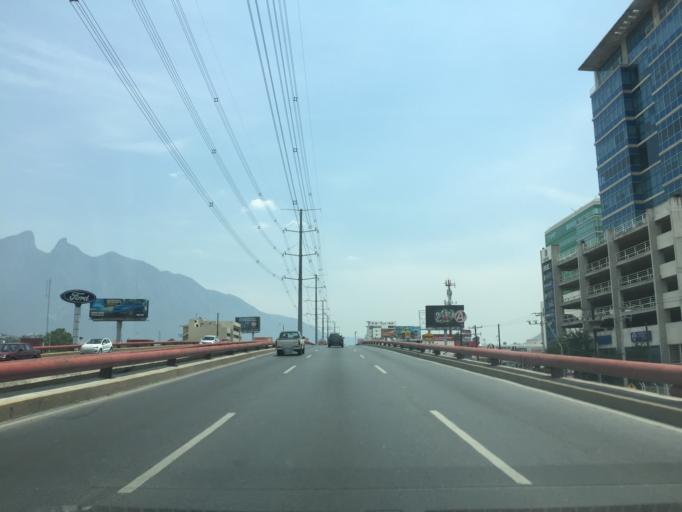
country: MX
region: Nuevo Leon
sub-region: Monterrey
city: Monterrey
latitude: 25.6320
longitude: -100.3023
